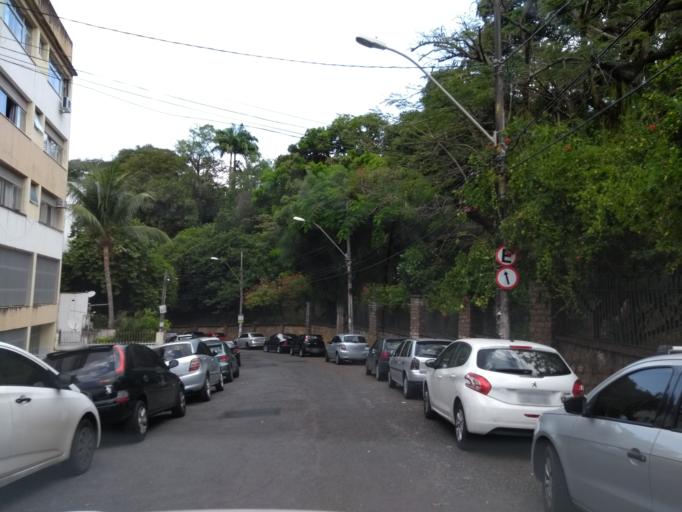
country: BR
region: Bahia
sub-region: Salvador
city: Salvador
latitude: -13.0005
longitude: -38.5302
